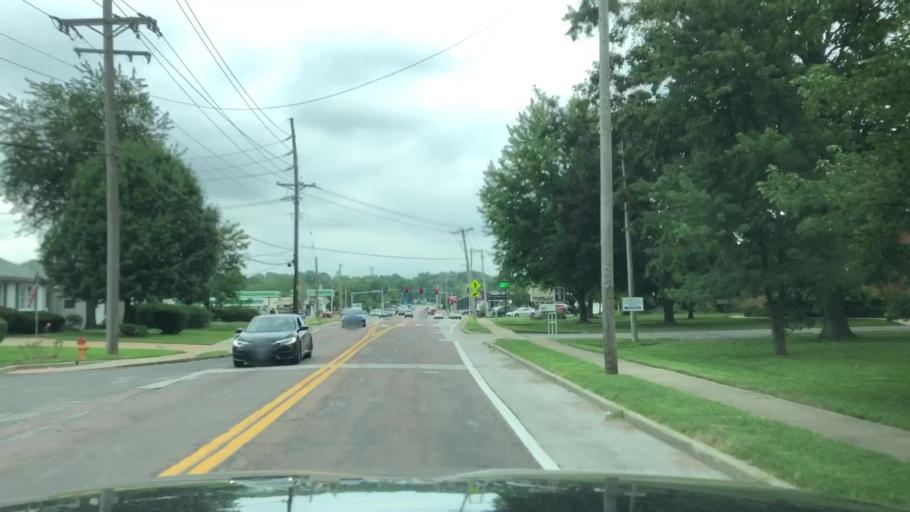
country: US
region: Missouri
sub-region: Saint Louis County
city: Florissant
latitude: 38.7979
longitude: -90.3407
